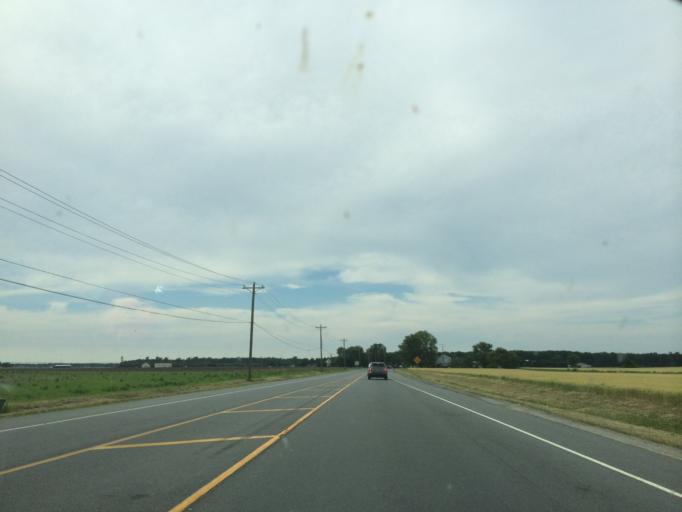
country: US
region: Delaware
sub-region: Sussex County
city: Bridgeville
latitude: 38.7546
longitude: -75.6293
